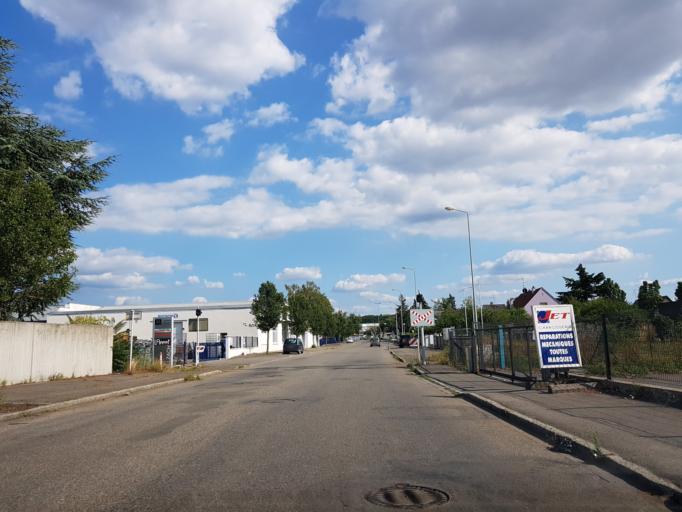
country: FR
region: Alsace
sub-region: Departement du Haut-Rhin
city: Riedisheim
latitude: 47.7633
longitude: 7.3708
